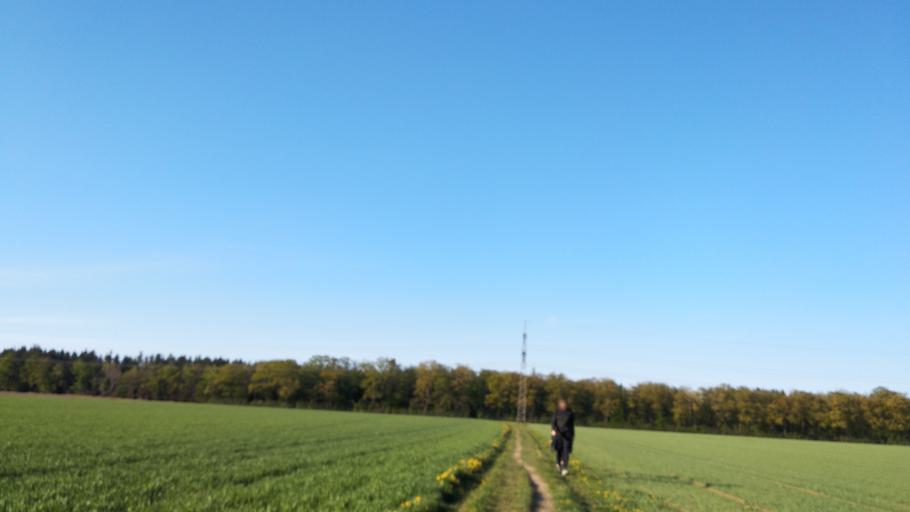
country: DE
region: Bavaria
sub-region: Upper Bavaria
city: Putzbrunn
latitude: 48.0873
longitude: 11.6973
